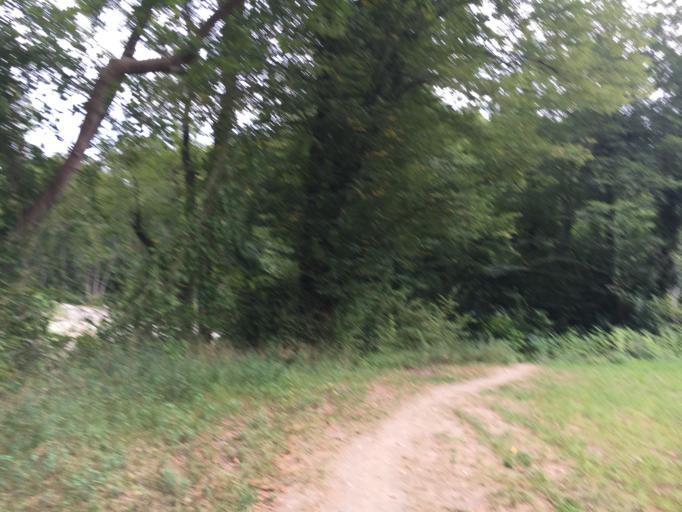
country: RU
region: Krasnodarskiy
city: Tuapse
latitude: 44.2574
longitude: 39.2197
